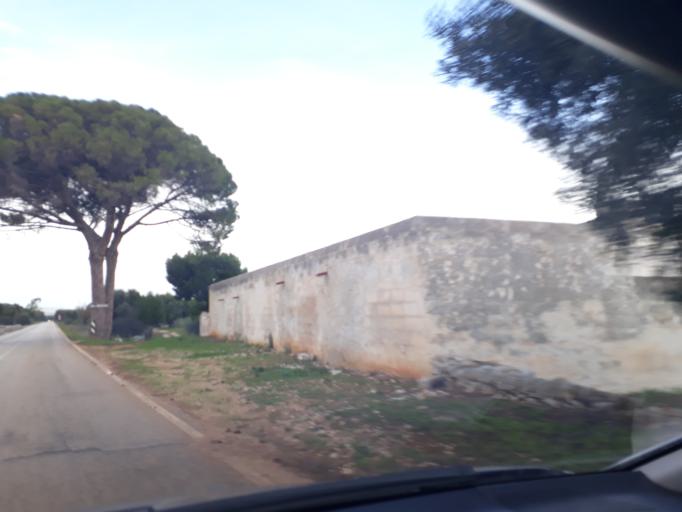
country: IT
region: Apulia
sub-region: Provincia di Brindisi
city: Pezze di Greco
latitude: 40.8066
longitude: 17.3905
